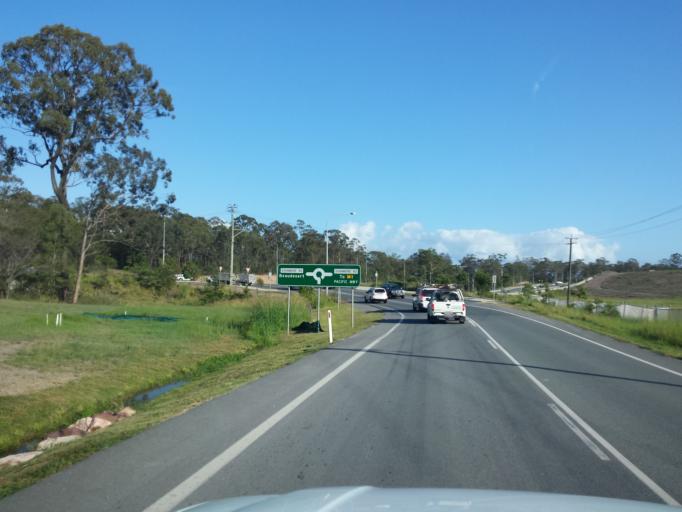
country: AU
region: Queensland
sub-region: Logan
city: Windaroo
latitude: -27.7607
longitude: 153.2134
